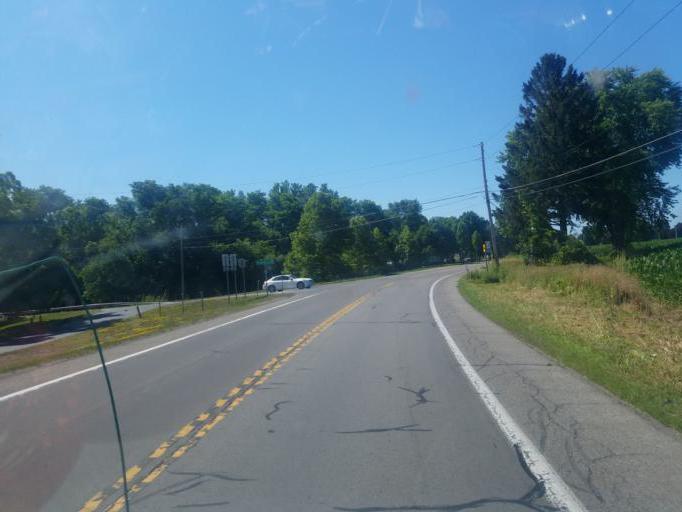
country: US
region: New York
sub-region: Ontario County
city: Phelps
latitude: 42.9880
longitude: -77.0885
